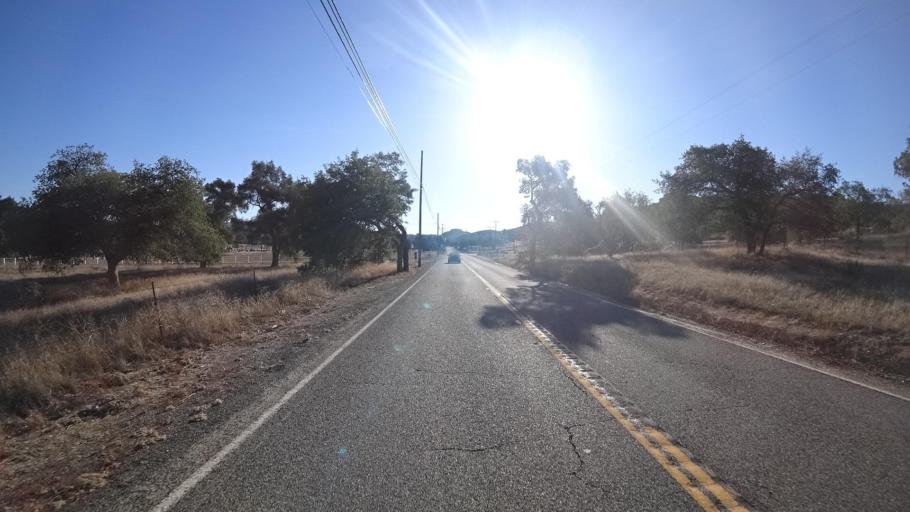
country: MX
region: Baja California
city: Tecate
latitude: 32.6063
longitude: -116.6190
